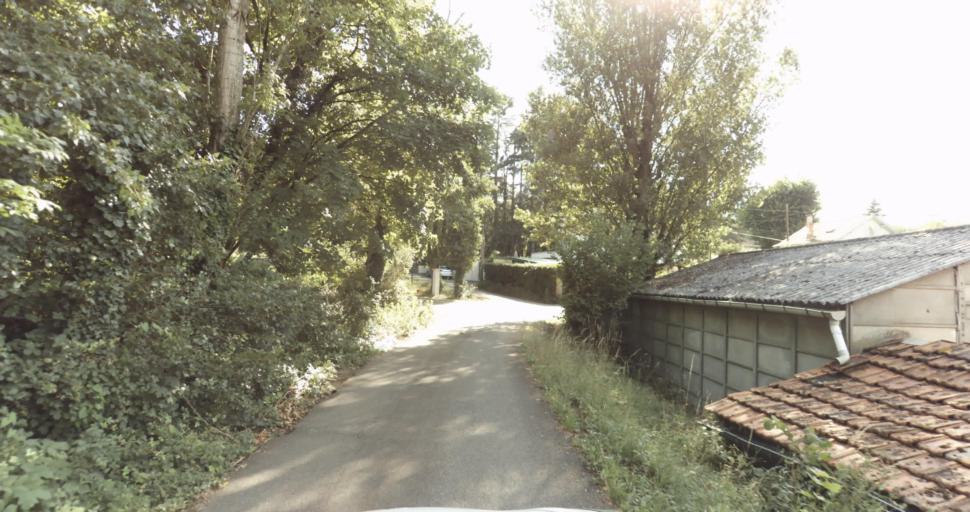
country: FR
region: Rhone-Alpes
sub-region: Departement du Rhone
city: Francheville
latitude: 45.7236
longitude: 4.7767
